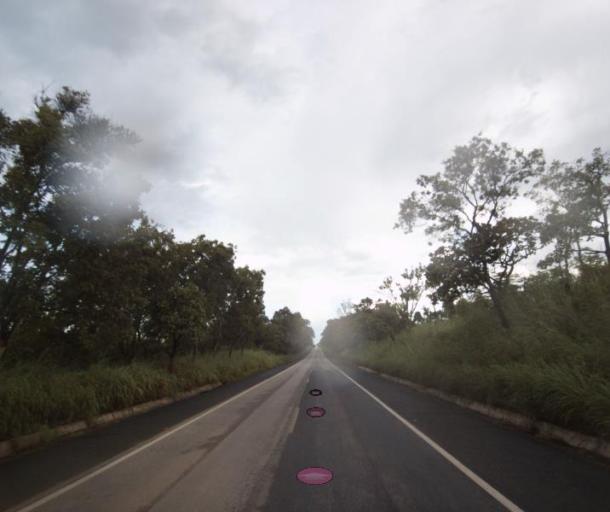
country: BR
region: Goias
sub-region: Porangatu
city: Porangatu
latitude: -13.9183
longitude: -49.0677
